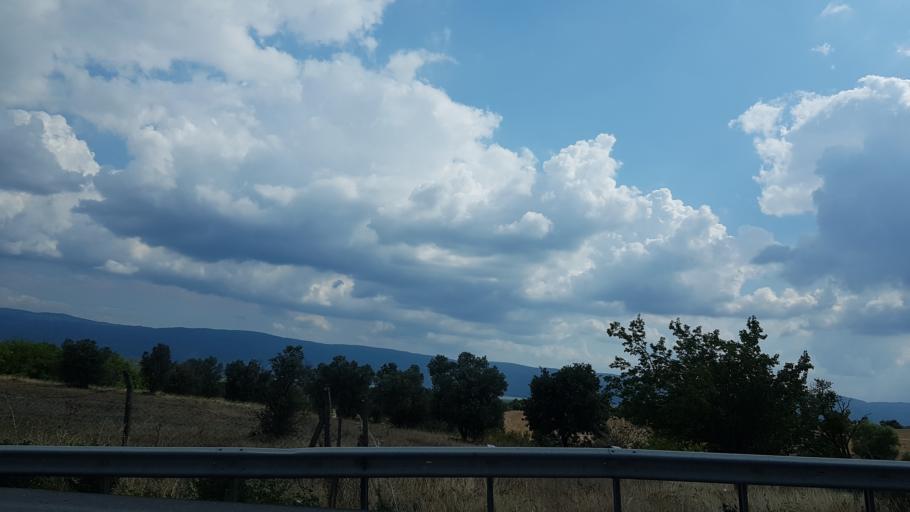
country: TR
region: Bursa
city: Mahmudiye
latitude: 40.2127
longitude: 28.6925
